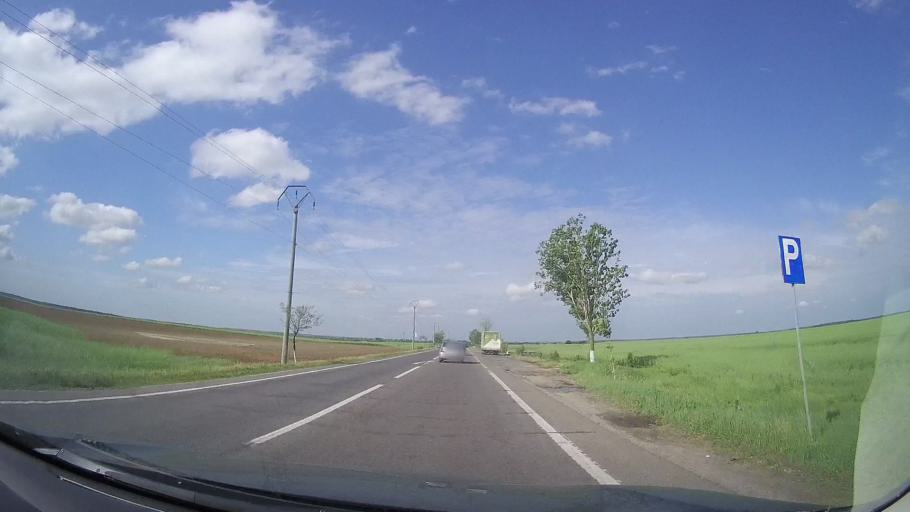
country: RO
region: Giurgiu
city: Iepuresti
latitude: 44.2971
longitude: 25.8816
